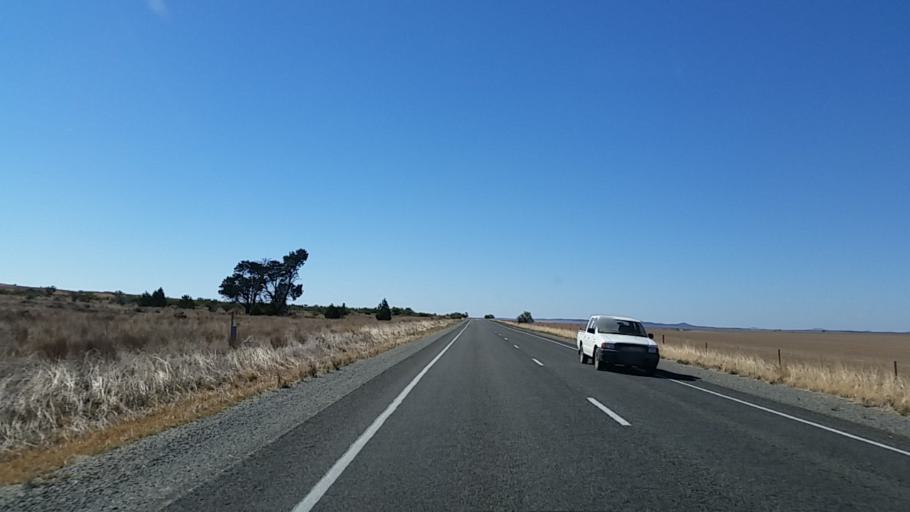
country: AU
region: South Australia
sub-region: Peterborough
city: Peterborough
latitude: -33.2177
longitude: 138.8933
